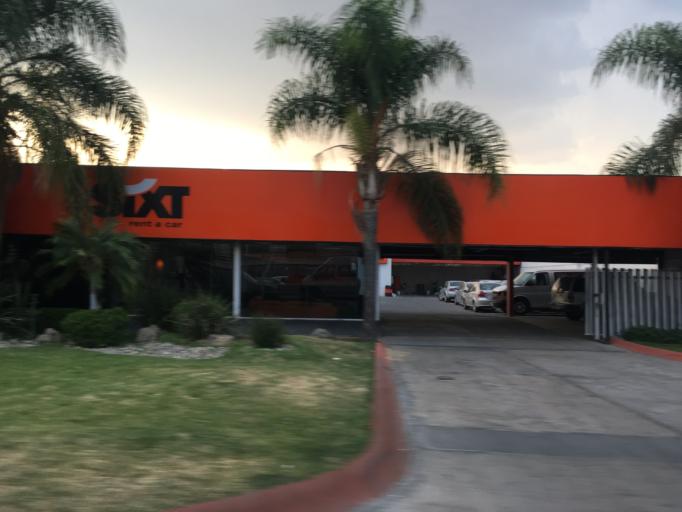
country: MX
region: Jalisco
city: El Quince
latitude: 20.5276
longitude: -103.3016
